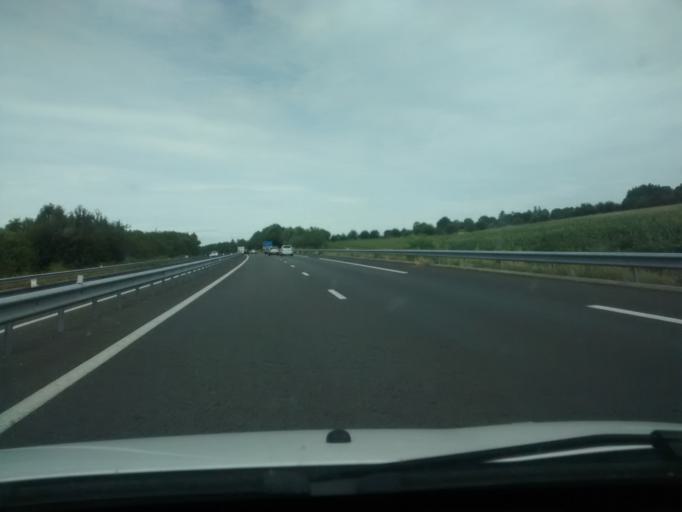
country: FR
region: Brittany
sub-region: Departement d'Ille-et-Vilaine
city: Saint-Etienne-en-Cogles
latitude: 48.4209
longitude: -1.3124
